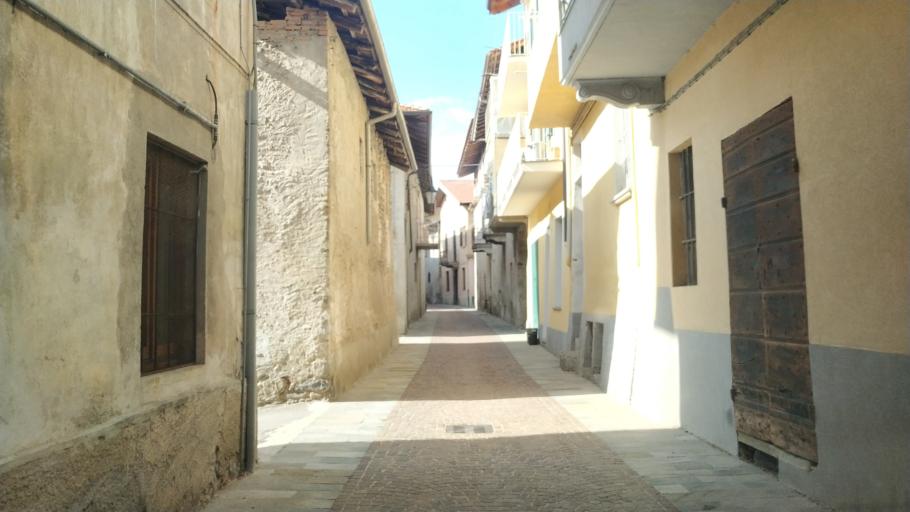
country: IT
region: Piedmont
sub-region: Provincia di Novara
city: Prato Sesia
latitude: 45.6481
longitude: 8.3770
